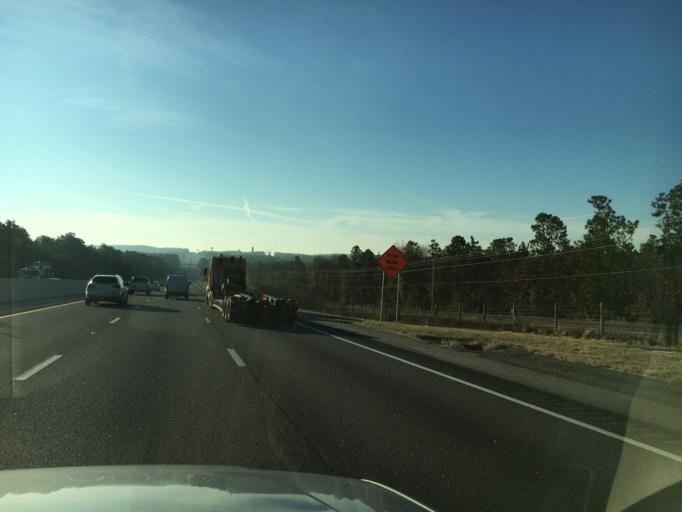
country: US
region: South Carolina
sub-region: Lexington County
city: Gaston
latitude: 33.8602
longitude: -81.0304
